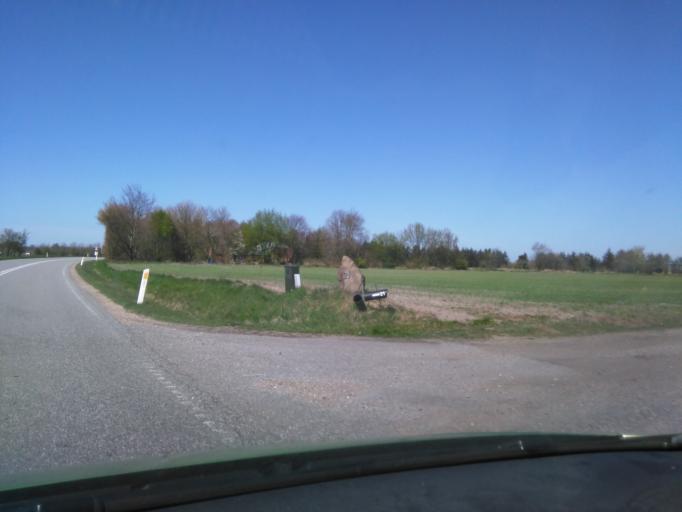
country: DK
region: South Denmark
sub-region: Billund Kommune
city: Grindsted
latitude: 55.7010
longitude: 8.7711
